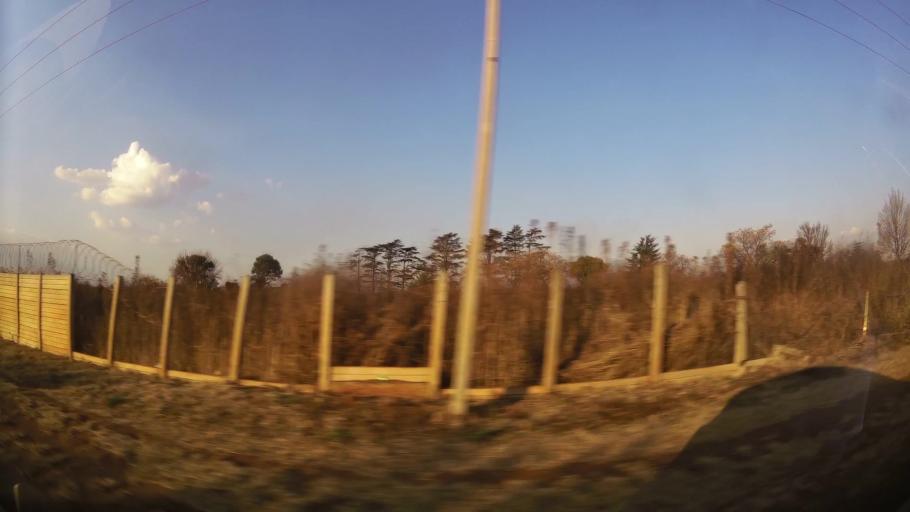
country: ZA
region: Gauteng
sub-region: Ekurhuleni Metropolitan Municipality
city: Germiston
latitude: -26.2967
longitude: 28.2311
